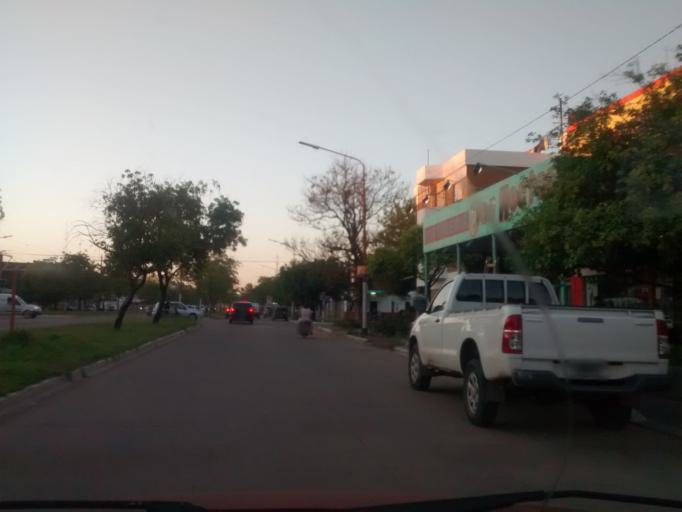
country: AR
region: Chaco
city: Resistencia
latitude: -27.4546
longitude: -58.9966
